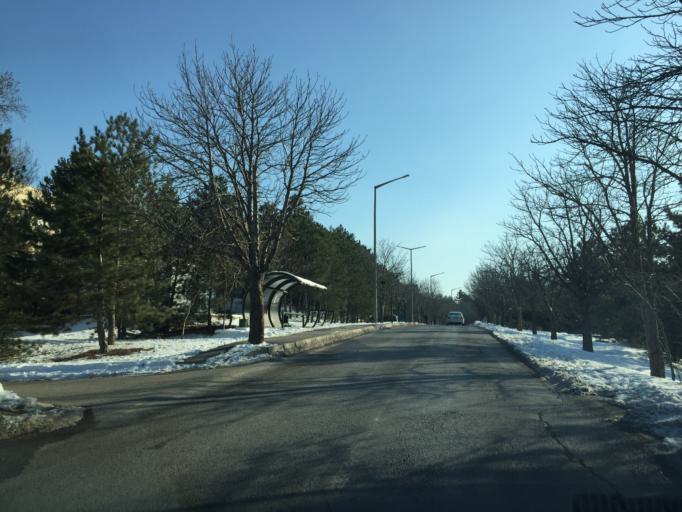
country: TR
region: Ankara
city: Ankara
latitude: 39.8904
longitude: 32.7813
